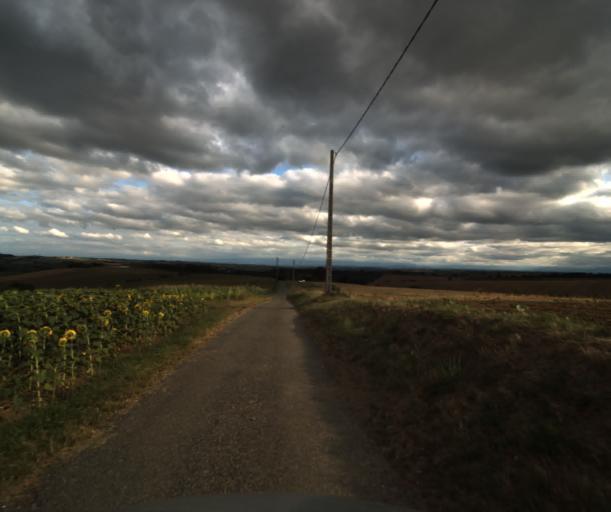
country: FR
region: Midi-Pyrenees
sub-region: Departement de la Haute-Garonne
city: Le Fauga
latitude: 43.3980
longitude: 1.3161
